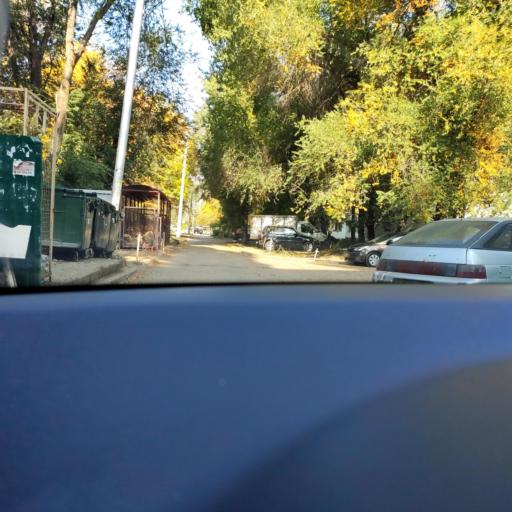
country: RU
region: Samara
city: Petra-Dubrava
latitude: 53.2440
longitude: 50.2622
